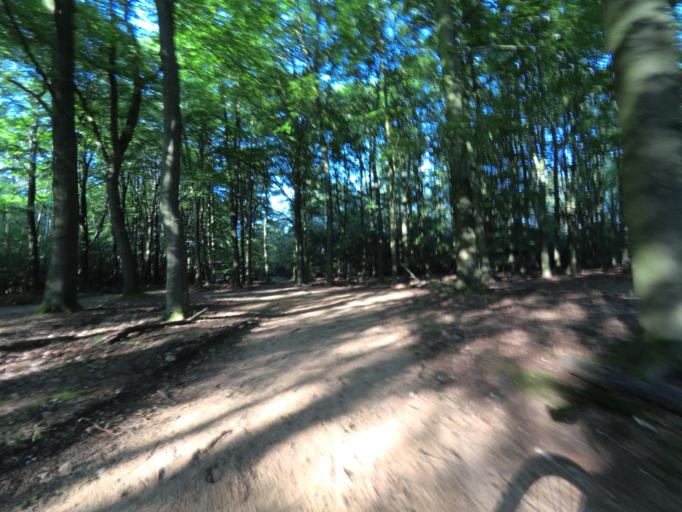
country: NL
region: Gelderland
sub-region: Gemeente Apeldoorn
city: Beekbergen
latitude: 52.1411
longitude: 5.9128
